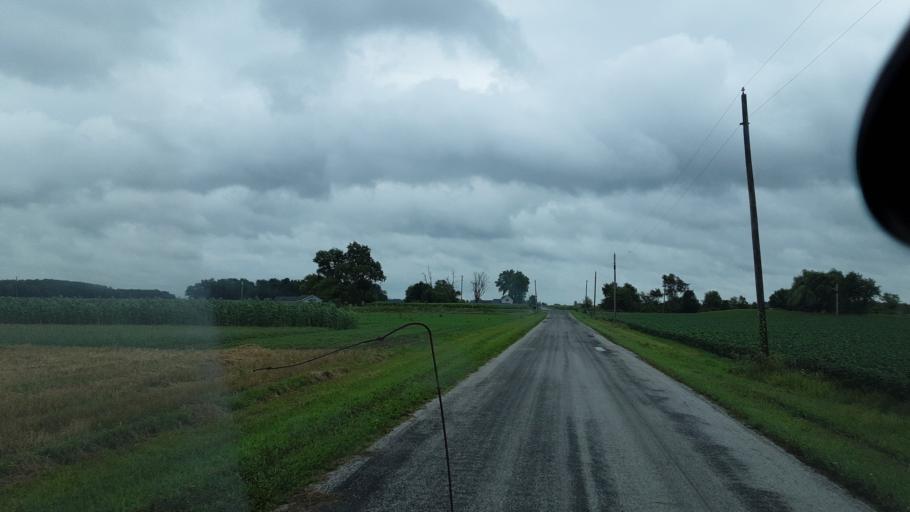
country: US
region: Indiana
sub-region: Wells County
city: Bluffton
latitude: 40.7883
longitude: -85.0717
